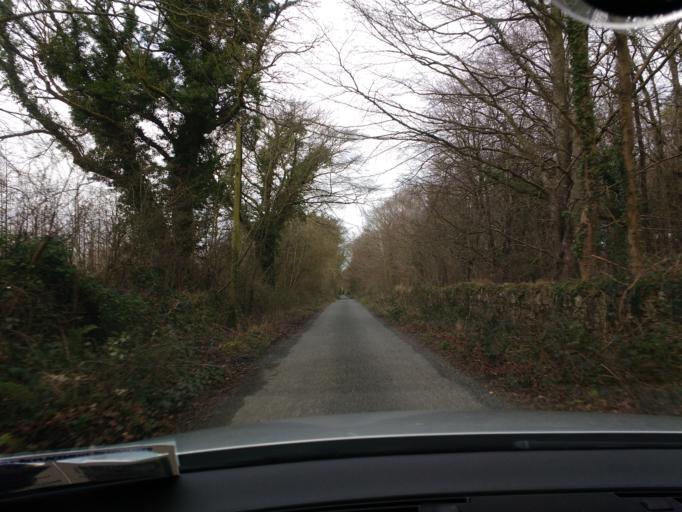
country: IE
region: Leinster
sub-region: Laois
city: Rathdowney
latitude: 52.6630
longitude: -7.5608
